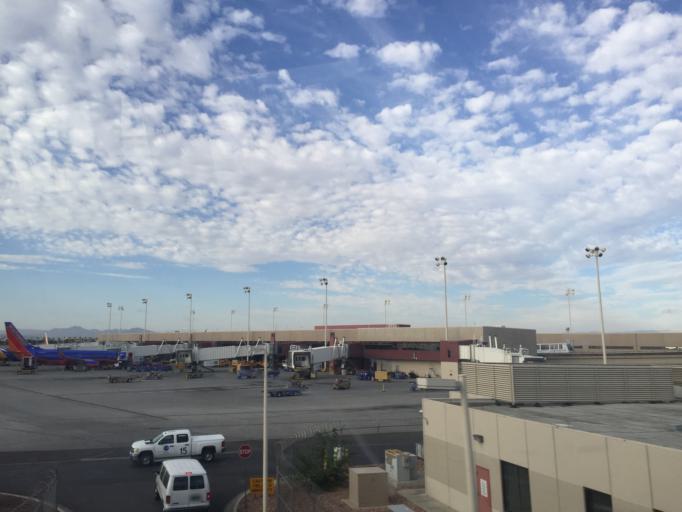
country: US
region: Nevada
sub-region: Clark County
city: Paradise
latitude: 36.0828
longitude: -115.1466
